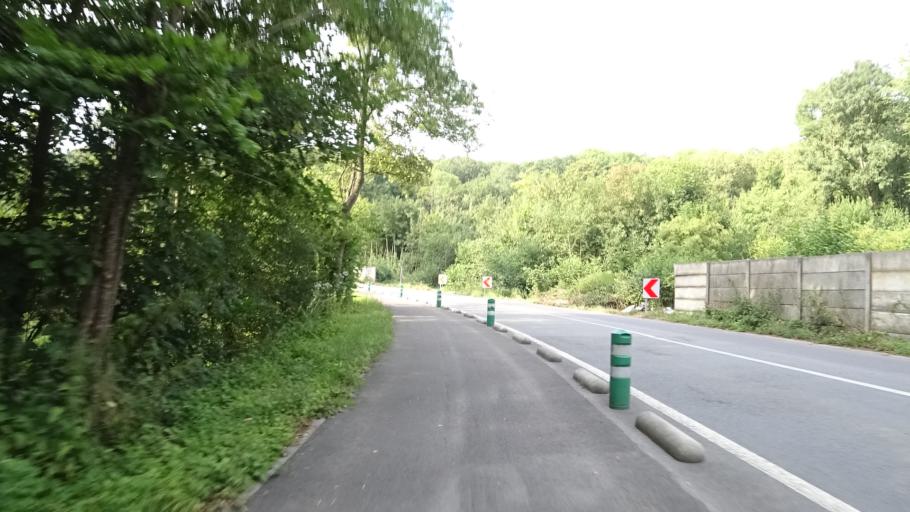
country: BE
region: Wallonia
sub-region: Province de Namur
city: Namur
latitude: 50.4859
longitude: 4.8775
